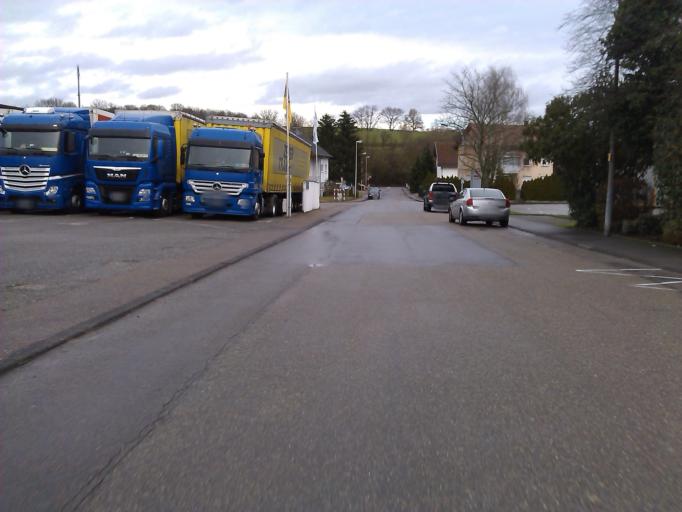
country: DE
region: Baden-Wuerttemberg
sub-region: Regierungsbezirk Stuttgart
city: Bad Wimpfen
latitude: 49.1892
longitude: 9.1508
